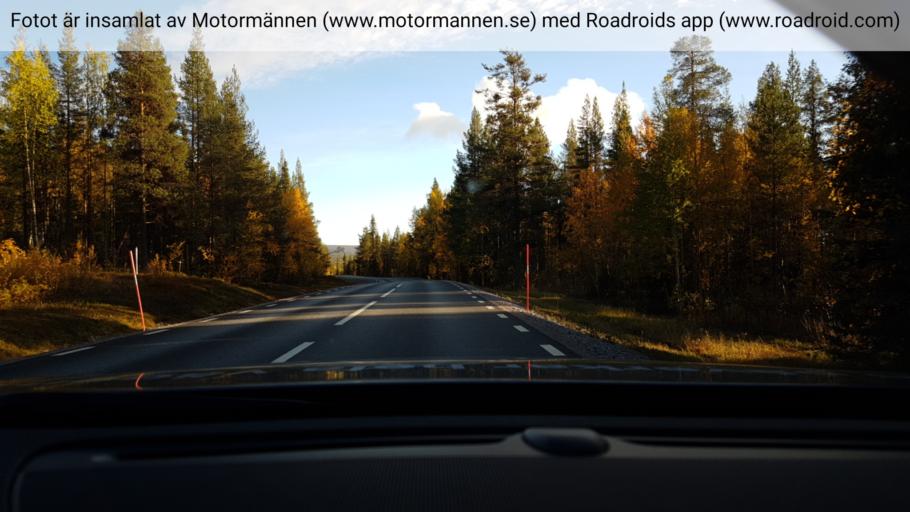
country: SE
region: Norrbotten
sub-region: Jokkmokks Kommun
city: Jokkmokk
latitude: 66.9352
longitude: 19.8182
